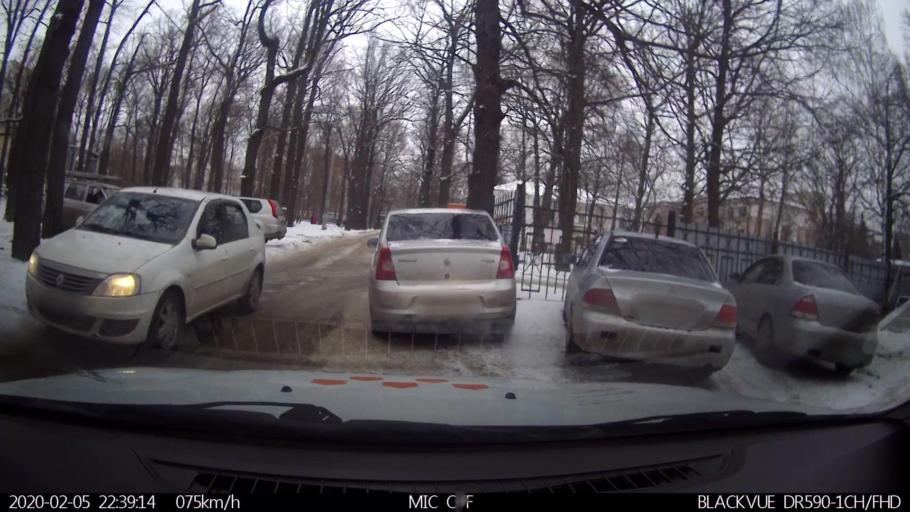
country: RU
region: Nizjnij Novgorod
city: Imeni Stepana Razina
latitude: 54.7264
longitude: 44.2926
